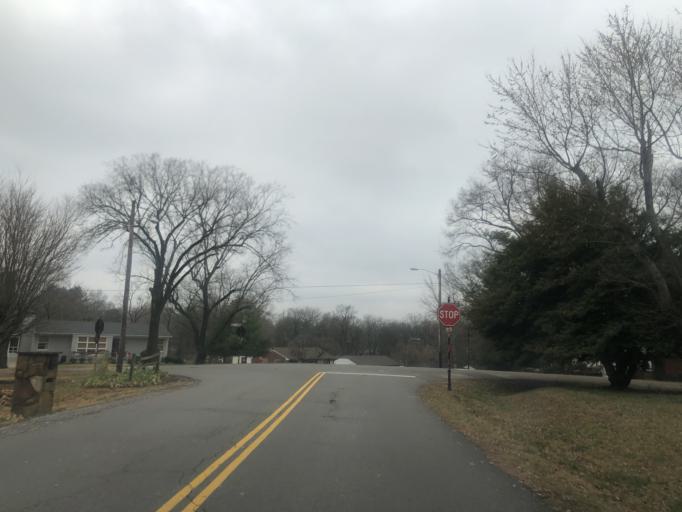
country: US
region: Tennessee
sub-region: Davidson County
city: Lakewood
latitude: 36.1706
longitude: -86.6917
